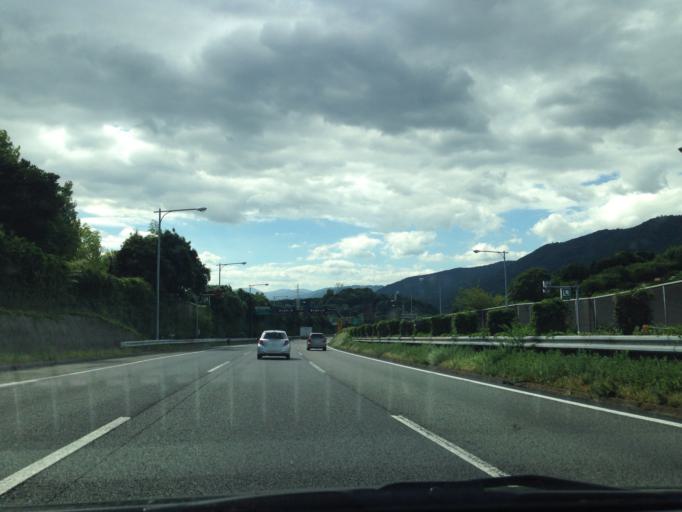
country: JP
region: Kanagawa
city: Hadano
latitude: 35.3404
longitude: 139.1620
